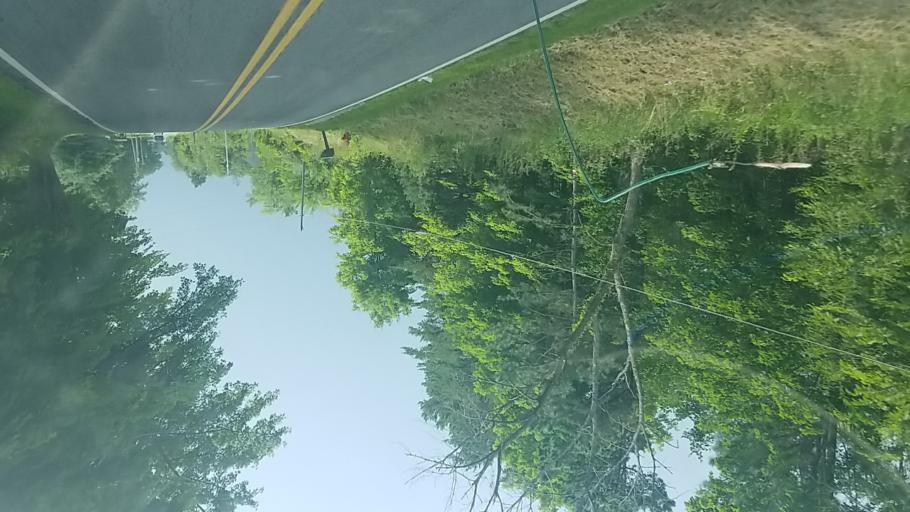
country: US
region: Ohio
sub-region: Medina County
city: Lodi
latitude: 41.0520
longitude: -82.0055
